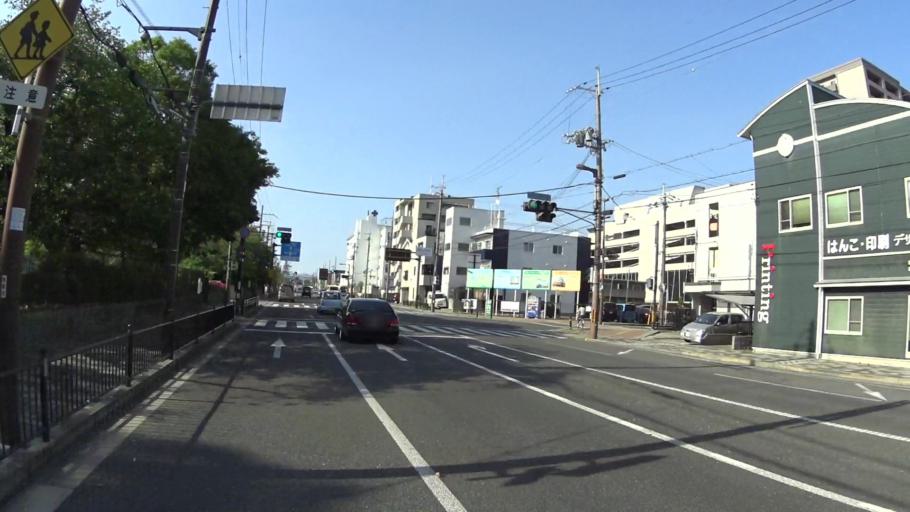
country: JP
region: Kyoto
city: Muko
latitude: 34.9221
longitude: 135.6979
